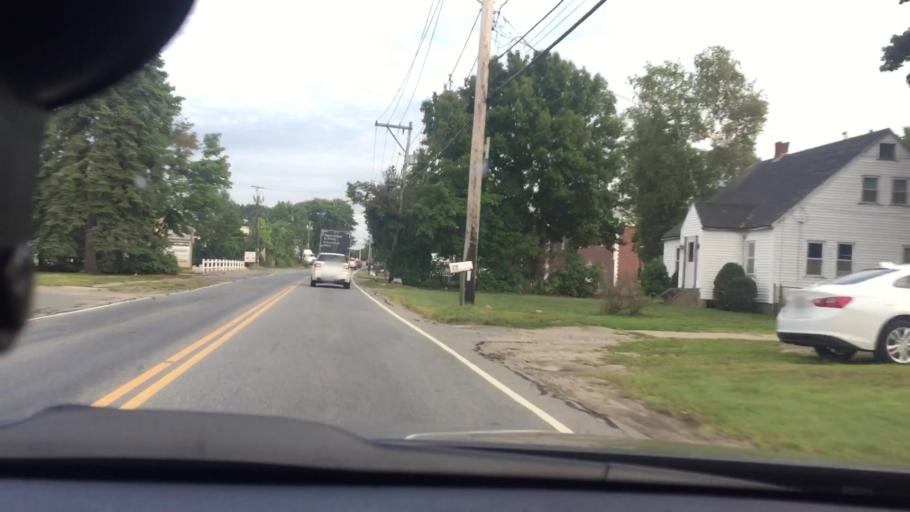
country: US
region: Massachusetts
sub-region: Norfolk County
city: Randolph
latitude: 42.1496
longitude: -71.0727
